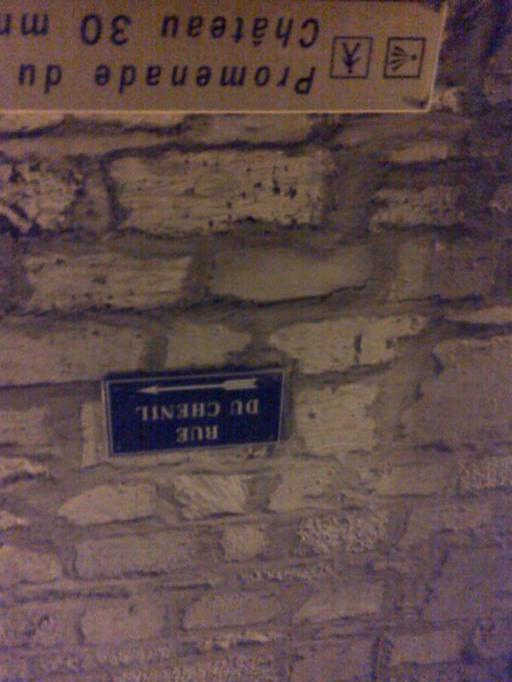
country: FR
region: Champagne-Ardenne
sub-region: Departement de la Haute-Marne
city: Joinville
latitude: 48.4437
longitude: 5.1370
